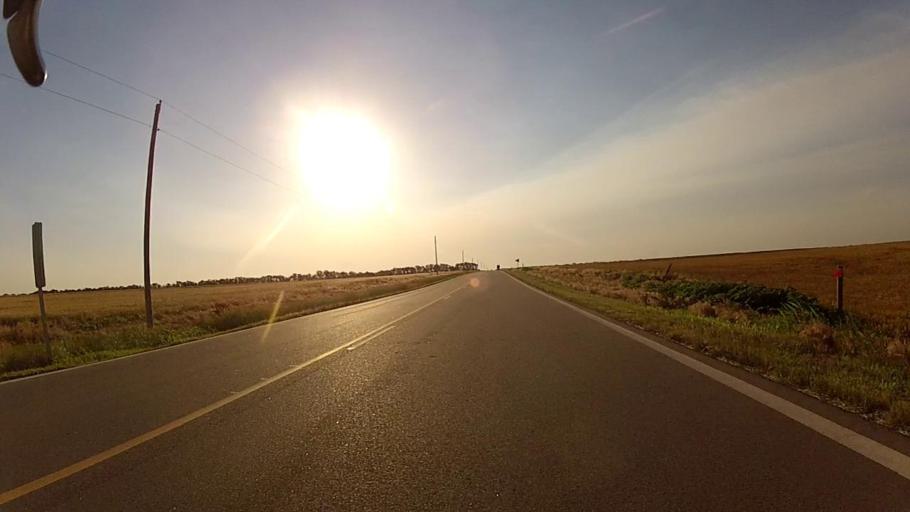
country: US
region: Kansas
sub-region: Sumner County
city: Caldwell
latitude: 37.1544
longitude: -97.7981
